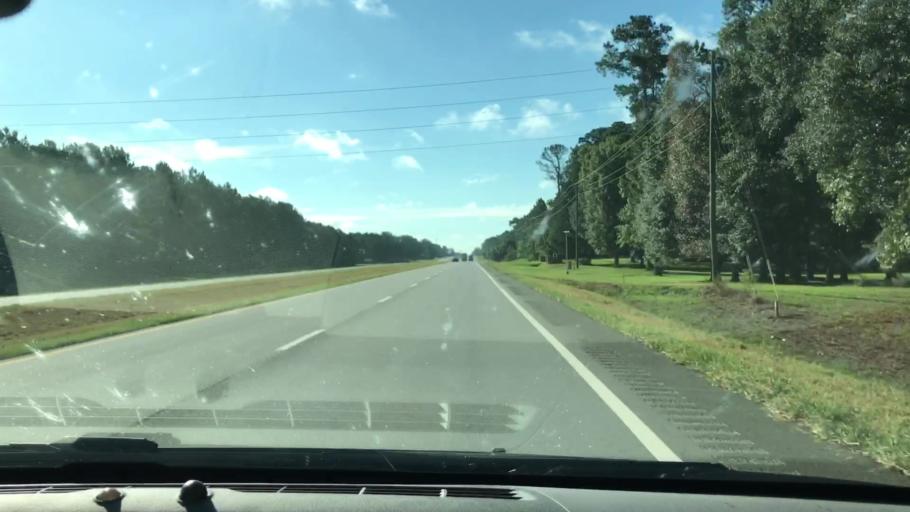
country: US
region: Georgia
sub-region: Lee County
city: Leesburg
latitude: 31.6758
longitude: -84.2945
